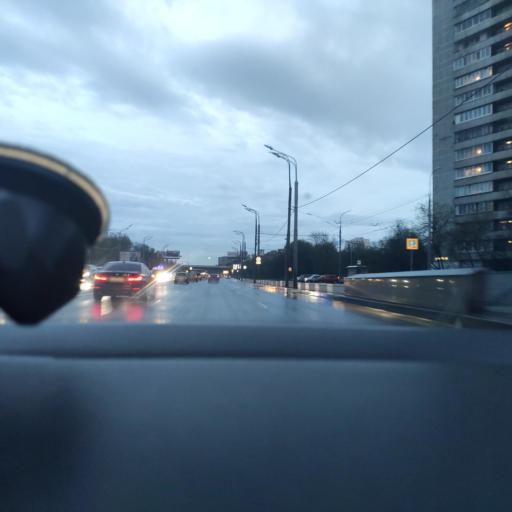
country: RU
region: Moscow
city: Pokrovskoye-Streshnevo
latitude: 55.8144
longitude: 37.4685
